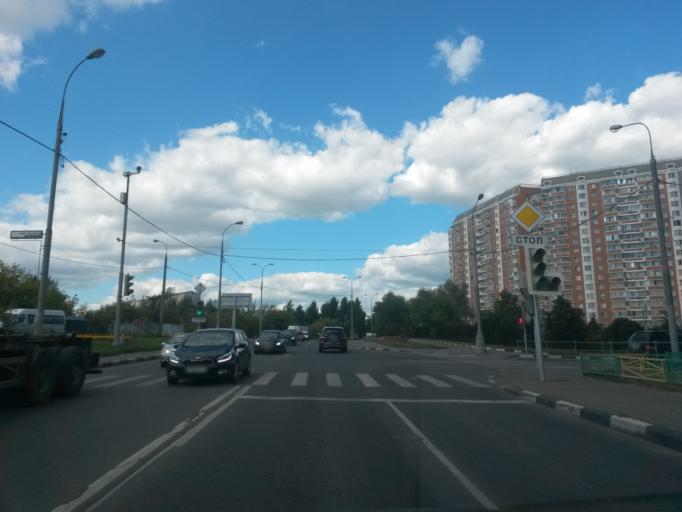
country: RU
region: Moscow
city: Tekstil'shchiki
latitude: 55.6881
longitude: 37.7172
